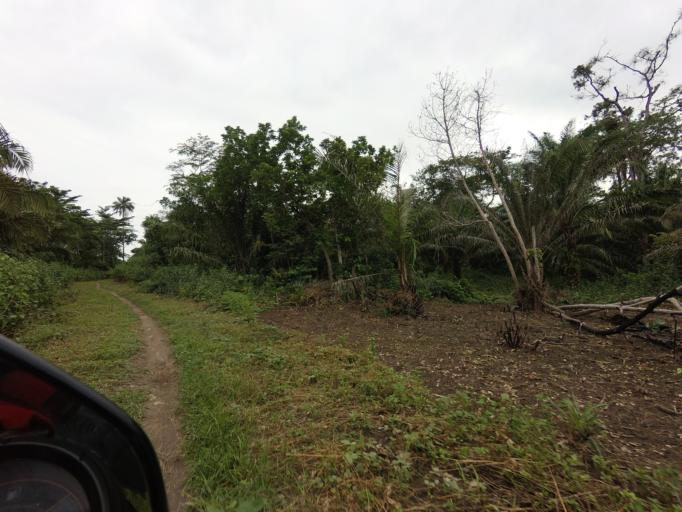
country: SL
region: Eastern Province
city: Mobai
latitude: 7.9798
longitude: -10.7099
